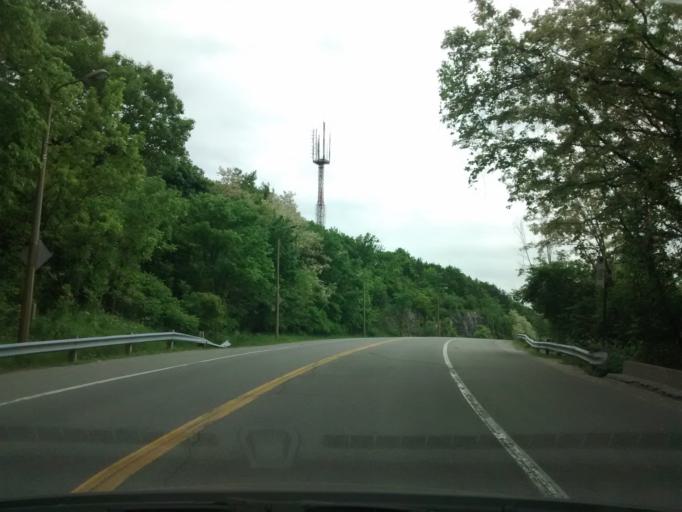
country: CA
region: Quebec
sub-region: Montreal
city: Montreal
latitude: 45.5088
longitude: -73.5911
